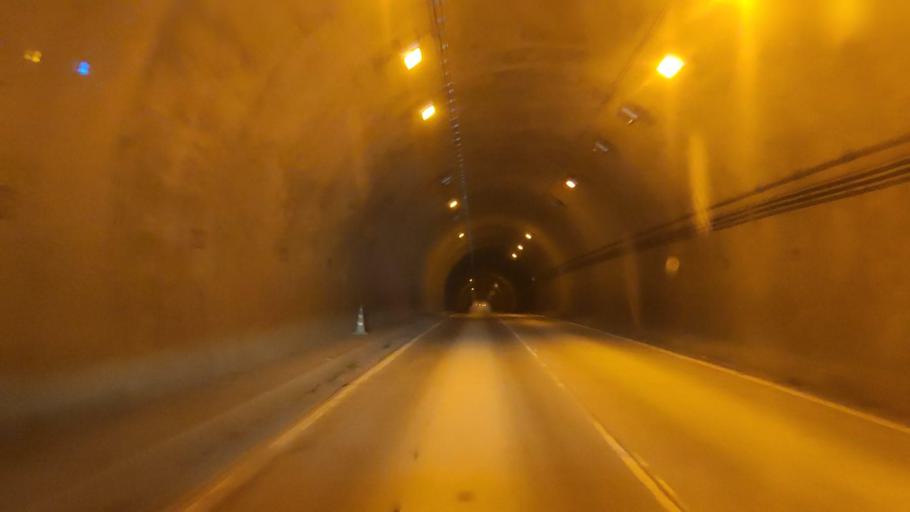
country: JP
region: Kumamoto
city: Hitoyoshi
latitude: 32.4166
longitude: 130.8450
